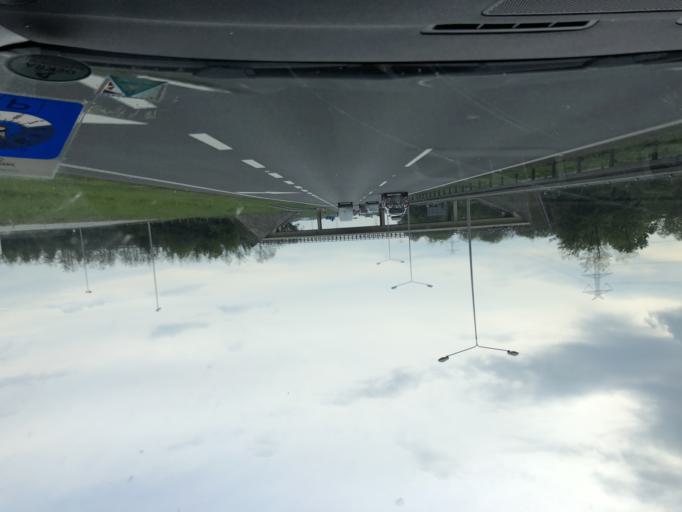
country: PL
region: Opole Voivodeship
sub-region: Powiat brzeski
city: Grodkow
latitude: 50.7835
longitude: 17.3463
